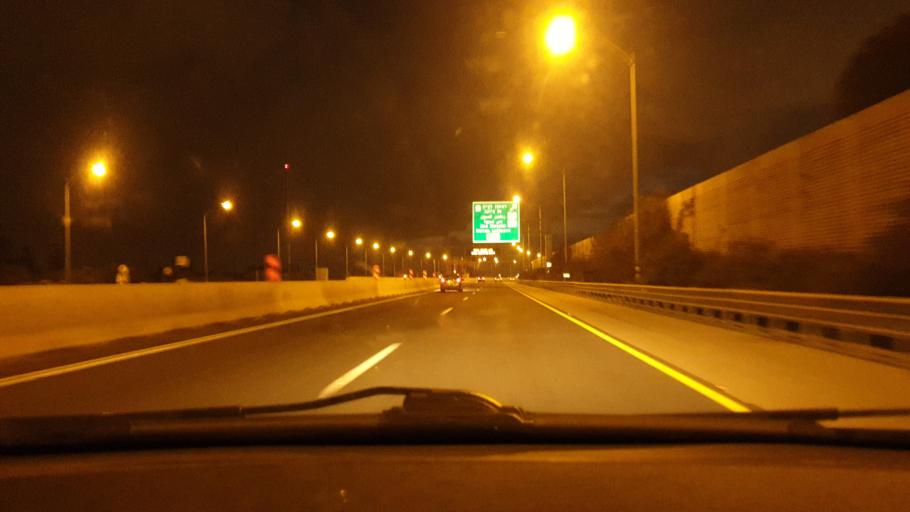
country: IL
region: Central District
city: Ness Ziona
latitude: 31.9296
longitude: 34.8243
